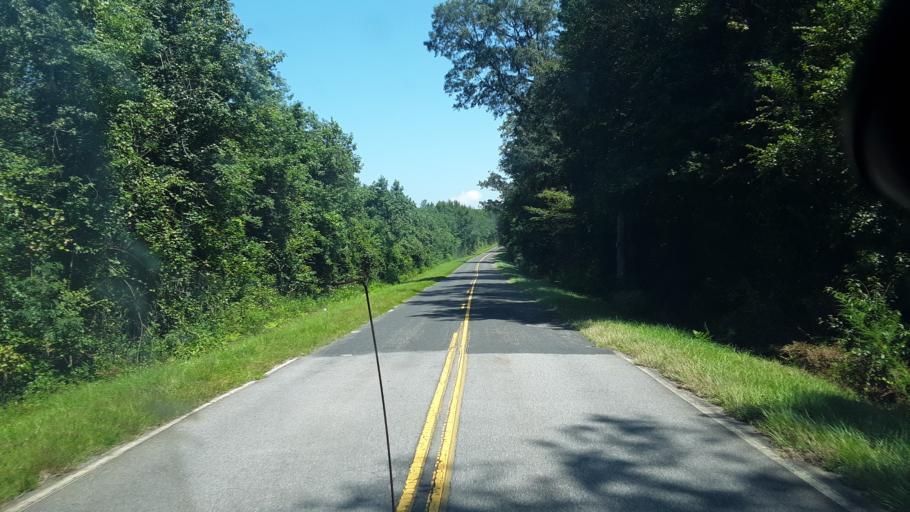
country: US
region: South Carolina
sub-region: Orangeburg County
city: Edisto
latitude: 33.5830
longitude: -81.0366
